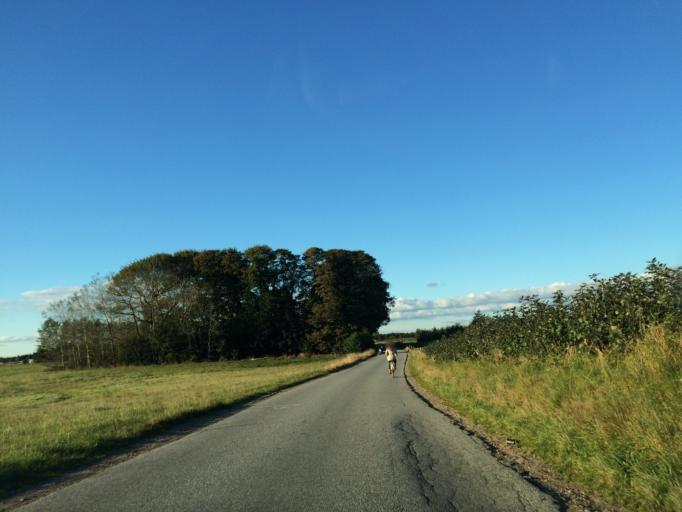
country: DK
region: Central Jutland
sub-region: Silkeborg Kommune
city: Svejbaek
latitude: 56.1779
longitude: 9.6929
